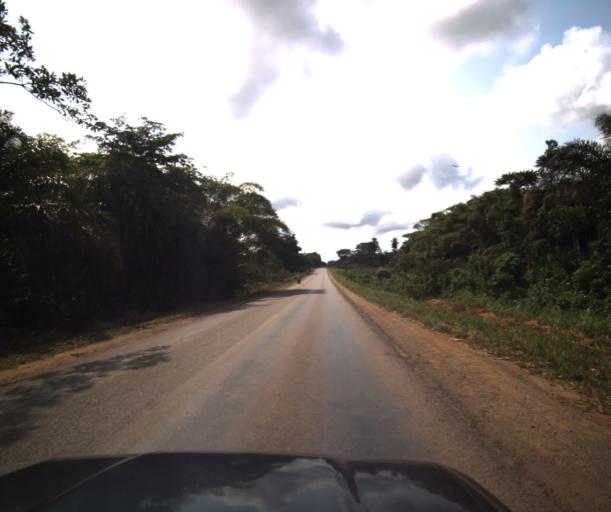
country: CM
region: Littoral
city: Edea
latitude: 3.7737
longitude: 10.1627
